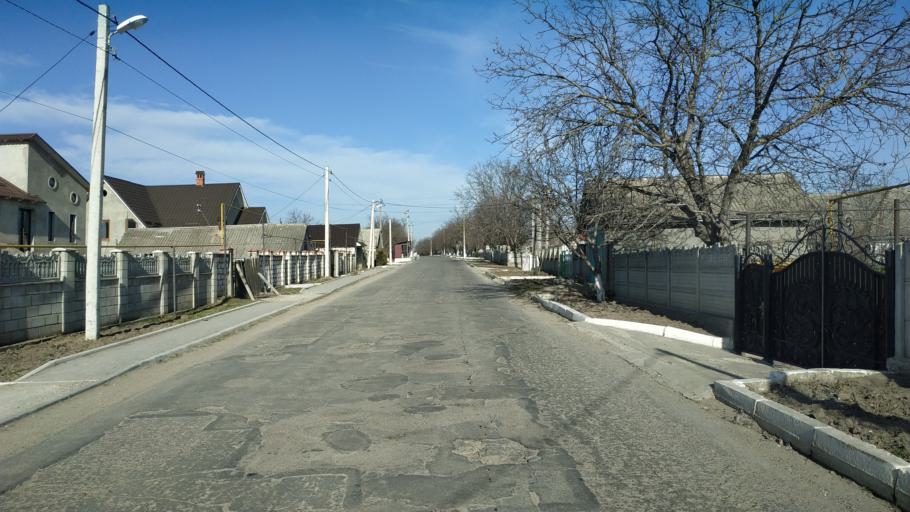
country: MD
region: Chisinau
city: Vatra
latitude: 47.0144
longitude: 28.6576
